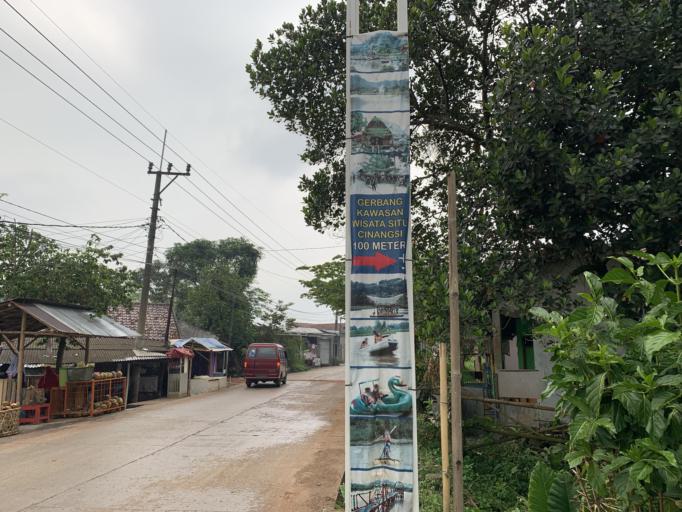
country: ID
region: West Java
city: Serpong
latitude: -6.3628
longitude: 106.5858
